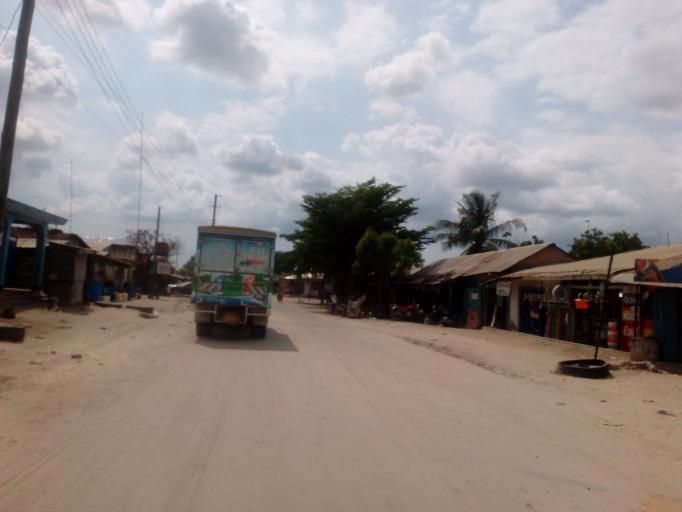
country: TZ
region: Dar es Salaam
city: Dar es Salaam
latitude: -6.8554
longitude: 39.2564
